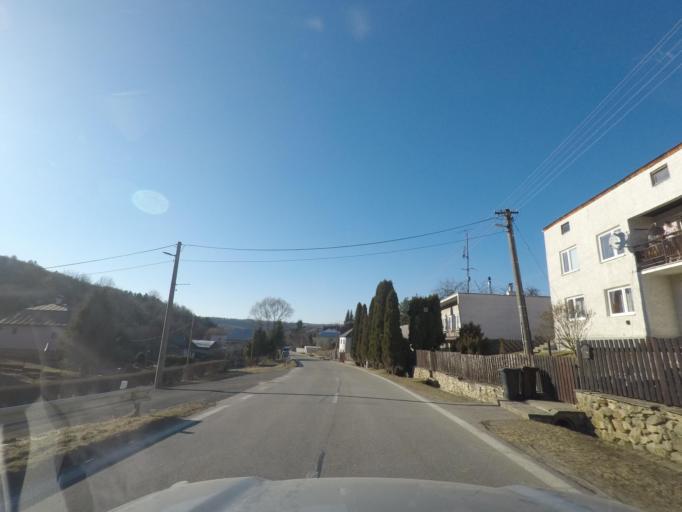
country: SK
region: Presovsky
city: Medzilaborce
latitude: 49.2461
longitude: 21.9328
